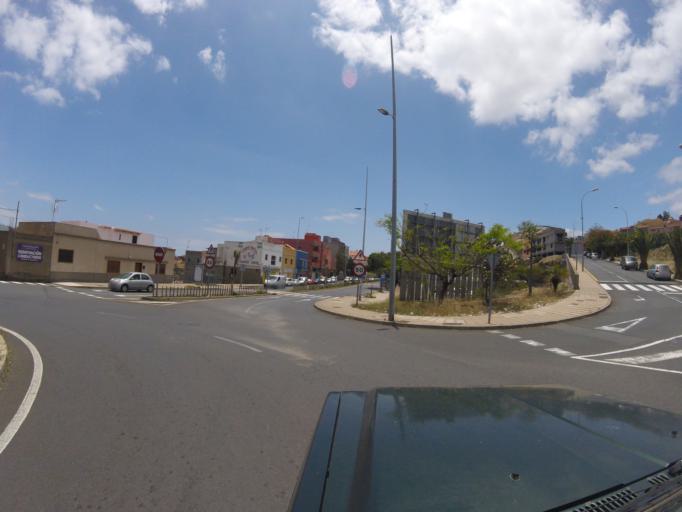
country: ES
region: Canary Islands
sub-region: Provincia de Santa Cruz de Tenerife
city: La Laguna
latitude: 28.4440
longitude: -16.3009
